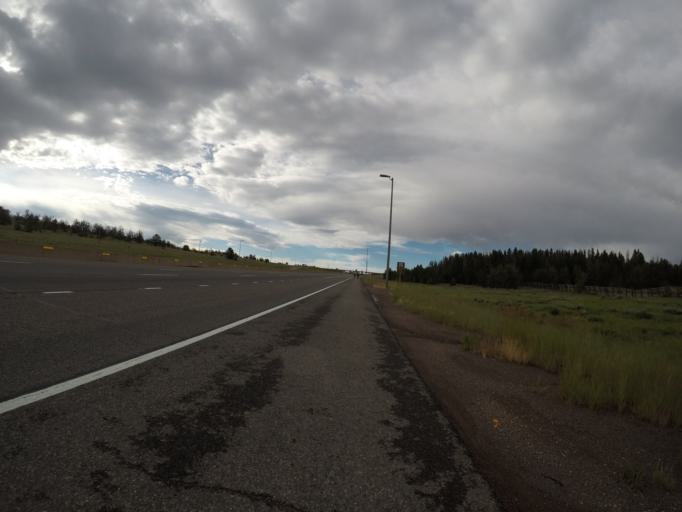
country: US
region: Wyoming
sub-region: Albany County
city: Laramie
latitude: 41.2447
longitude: -105.4410
